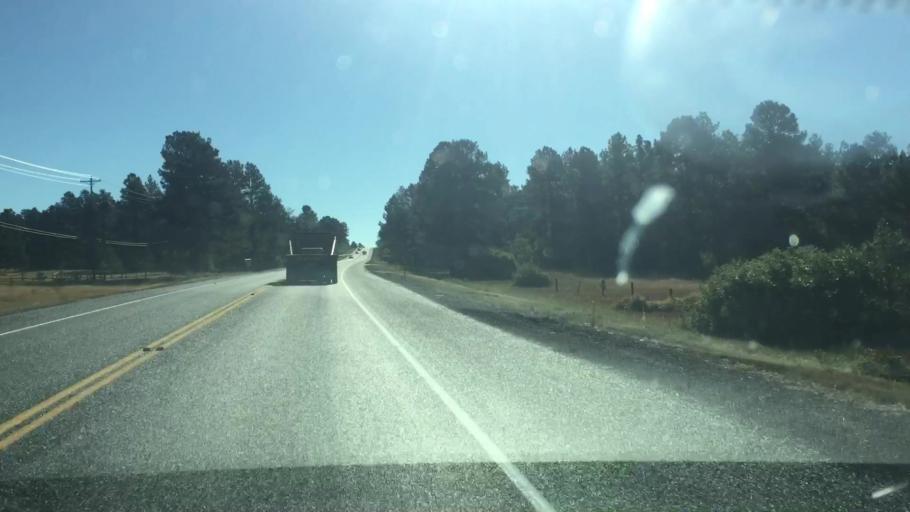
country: US
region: Colorado
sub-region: Douglas County
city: The Pinery
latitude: 39.3876
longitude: -104.7378
